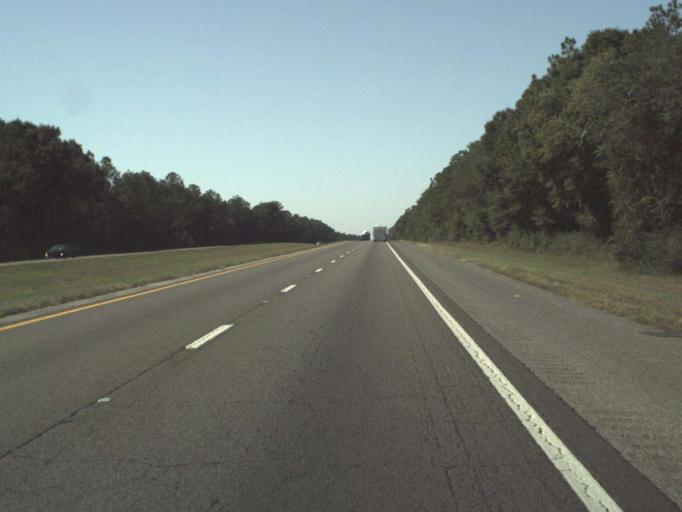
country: US
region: Florida
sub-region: Santa Rosa County
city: East Milton
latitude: 30.6549
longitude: -86.8807
